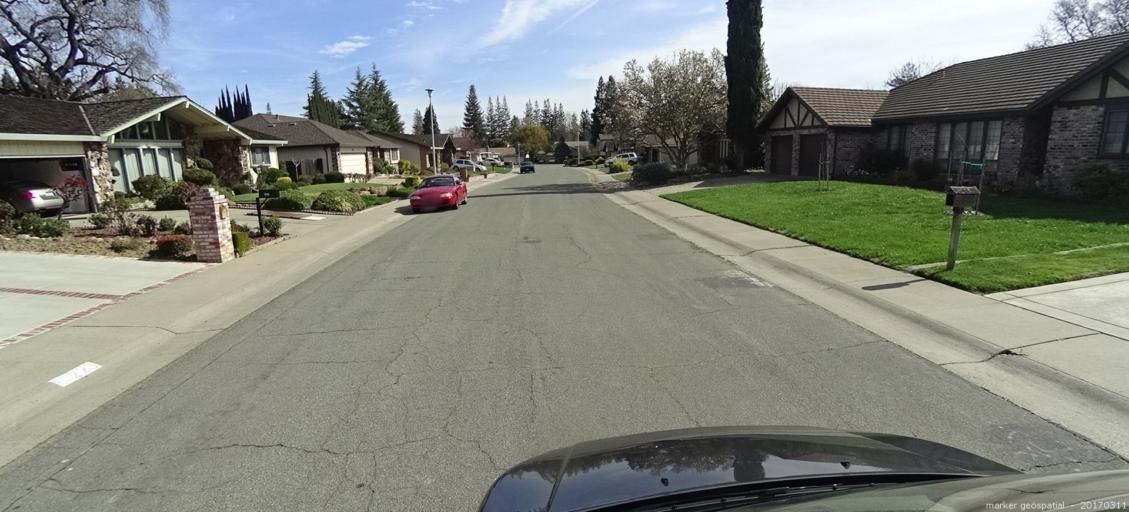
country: US
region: California
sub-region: Yolo County
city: West Sacramento
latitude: 38.4964
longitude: -121.5555
